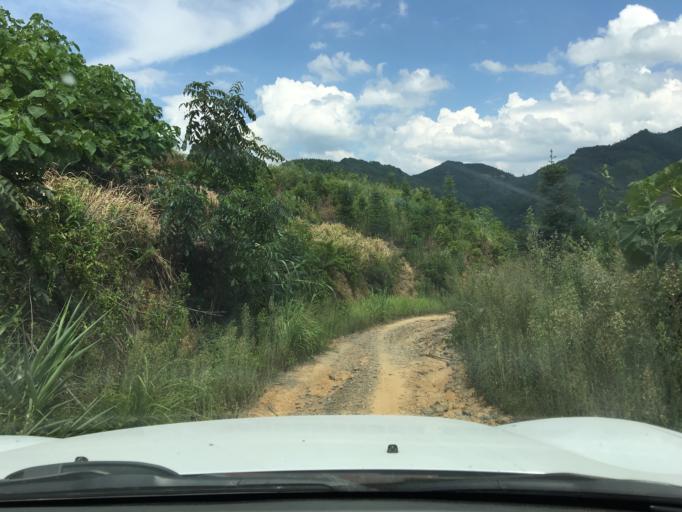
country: CN
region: Guangxi Zhuangzu Zizhiqu
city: Tongle
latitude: 24.9709
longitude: 105.9803
